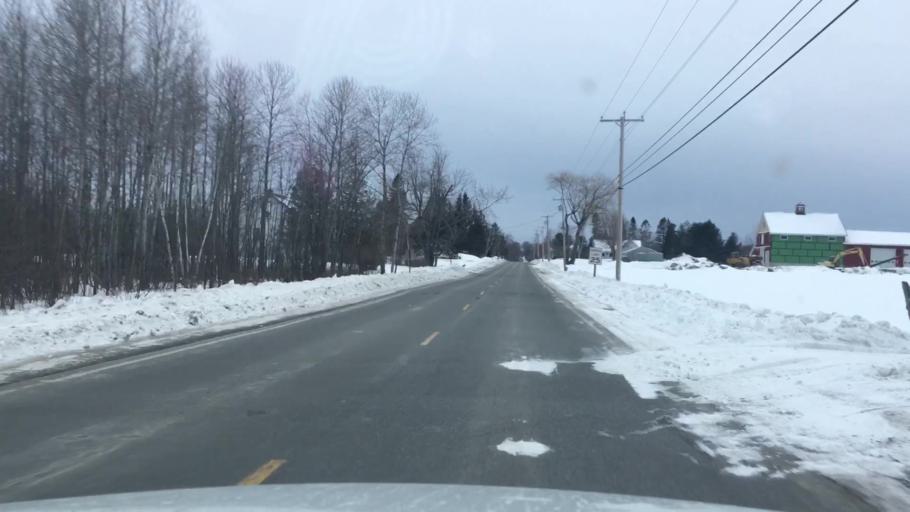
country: US
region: Maine
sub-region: Penobscot County
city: Corinna
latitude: 44.9252
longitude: -69.2503
